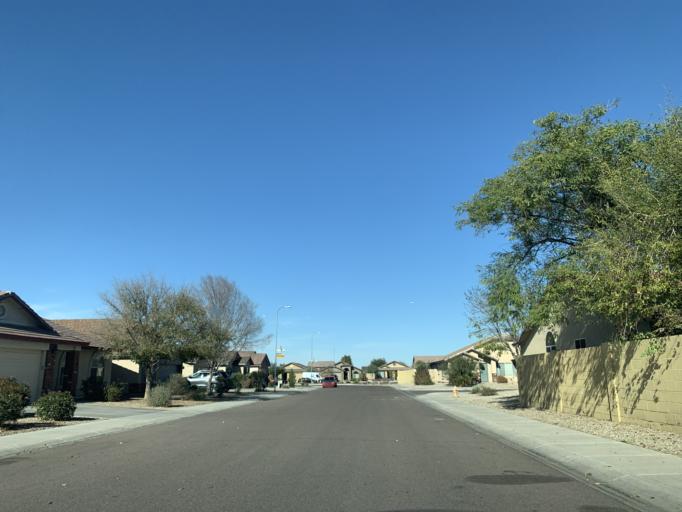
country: US
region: Arizona
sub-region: Maricopa County
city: Laveen
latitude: 33.3953
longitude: -112.1234
